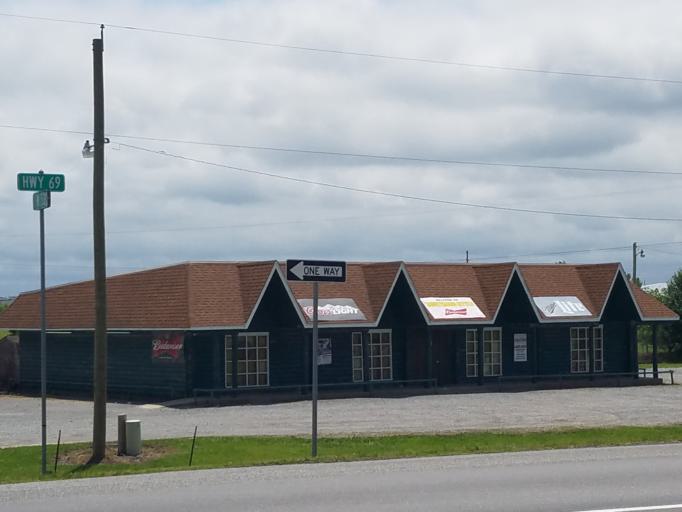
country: US
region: Oklahoma
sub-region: Mayes County
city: Pryor
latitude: 36.2494
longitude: -95.3358
